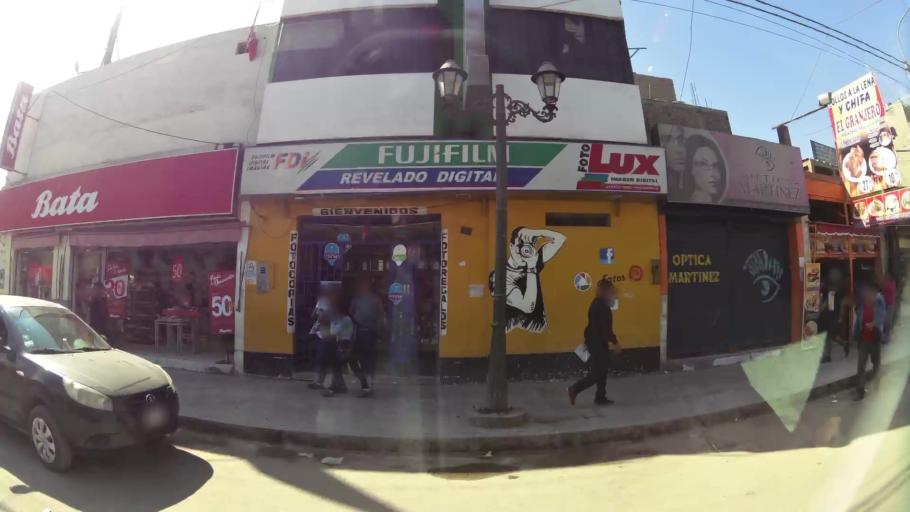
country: PE
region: Ica
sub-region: Provincia de Chincha
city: Chincha Alta
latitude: -13.4171
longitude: -76.1361
